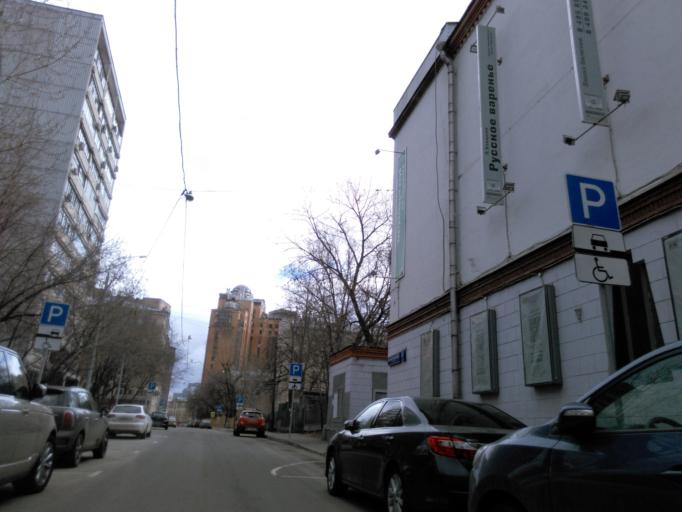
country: RU
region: Moskovskaya
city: Dorogomilovo
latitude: 55.7702
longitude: 37.5766
